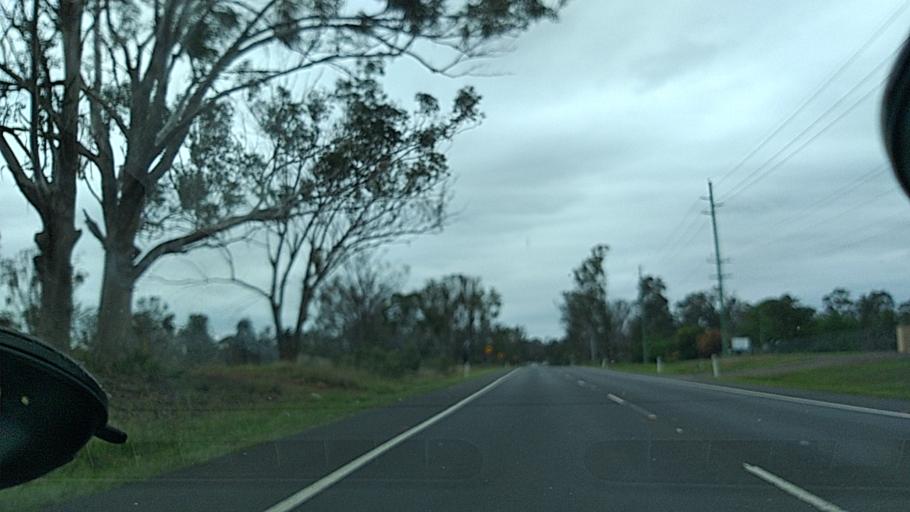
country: AU
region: New South Wales
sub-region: Penrith Municipality
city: Glenmore Park
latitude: -33.8229
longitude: 150.6846
